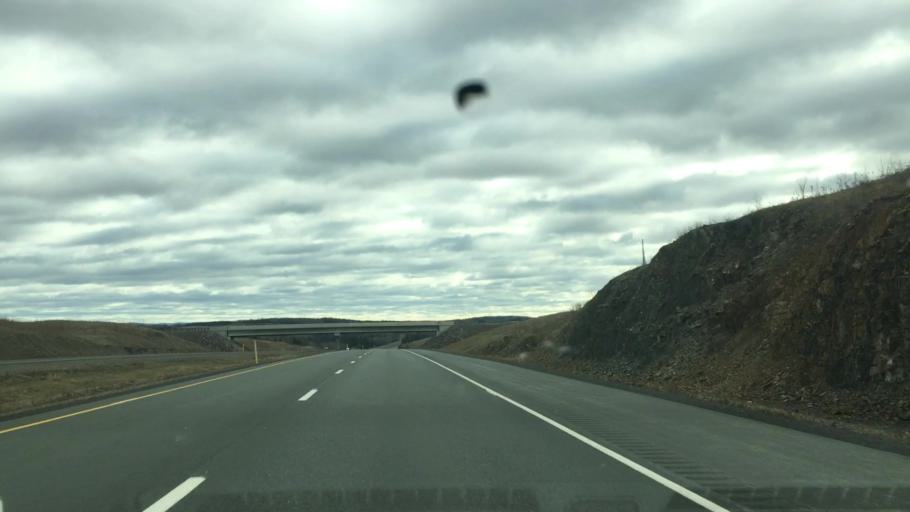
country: CA
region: New Brunswick
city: Florenceville-Bristol
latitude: 46.5488
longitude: -67.7306
